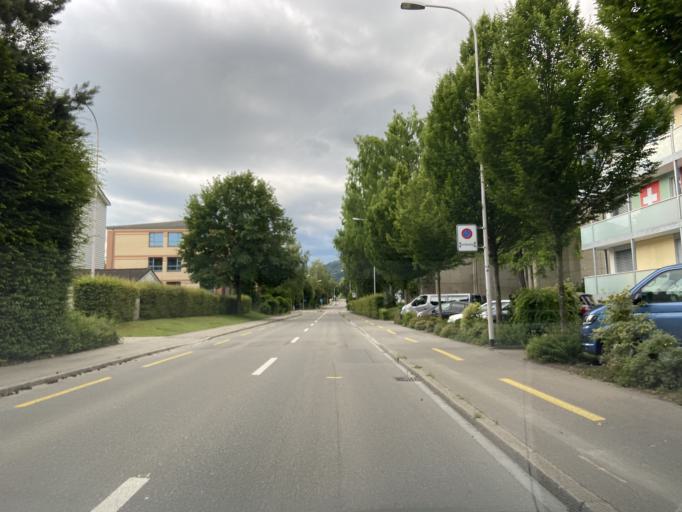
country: CH
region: Thurgau
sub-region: Muenchwilen District
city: Aadorf
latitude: 47.4938
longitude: 8.9042
